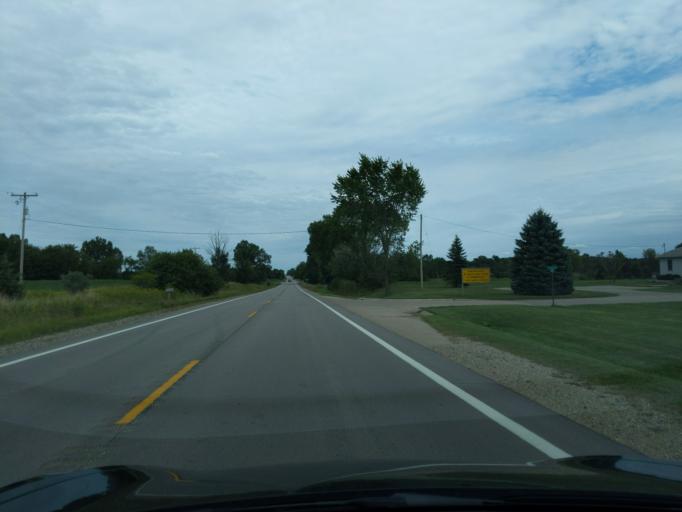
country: US
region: Michigan
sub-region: Barry County
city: Nashville
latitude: 42.5672
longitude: -85.0585
